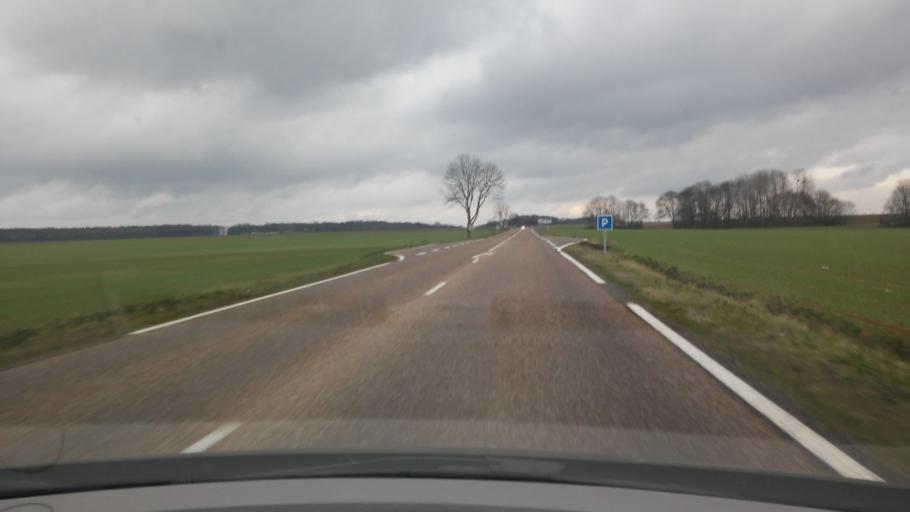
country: FR
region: Lorraine
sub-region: Departement de la Moselle
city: Retonfey
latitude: 49.1165
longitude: 6.3136
